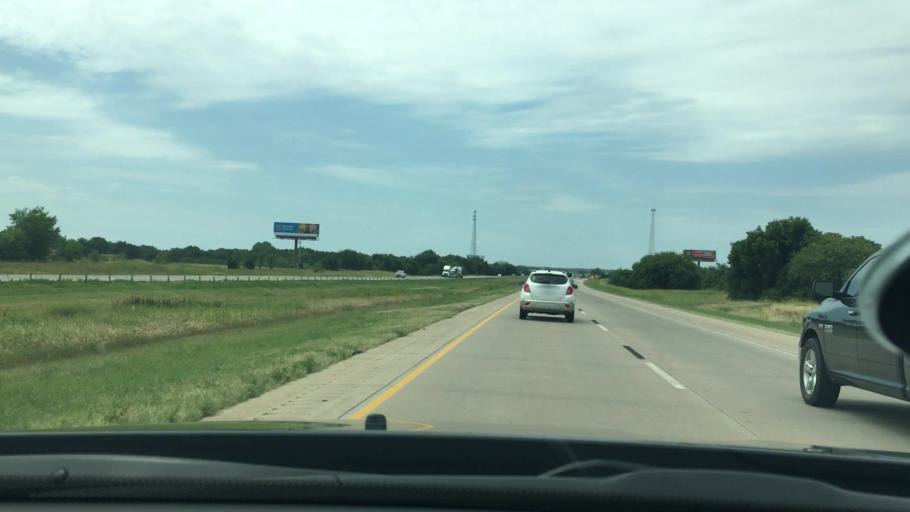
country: US
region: Oklahoma
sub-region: Carter County
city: Ardmore
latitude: 34.2832
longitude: -97.1602
